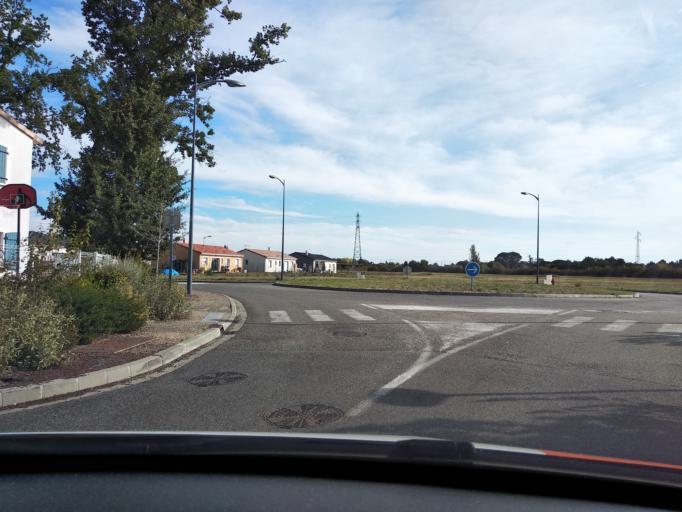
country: FR
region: Midi-Pyrenees
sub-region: Departement du Tarn-et-Garonne
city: Montauban
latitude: 44.0433
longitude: 1.3316
